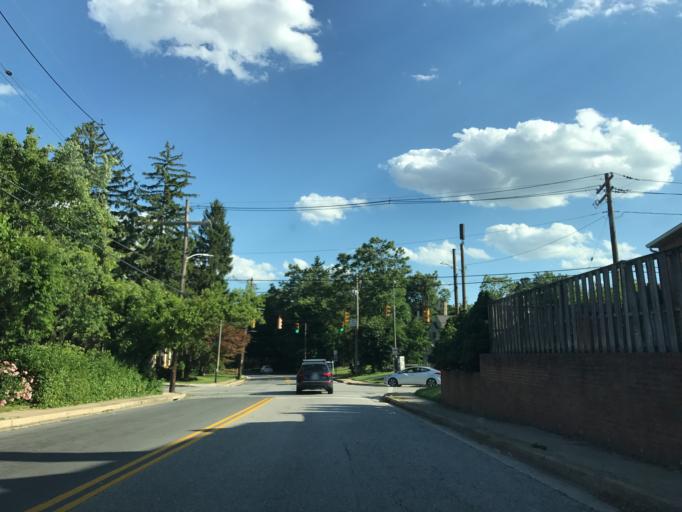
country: US
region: Maryland
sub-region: Baltimore County
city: Towson
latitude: 39.3687
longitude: -76.6181
